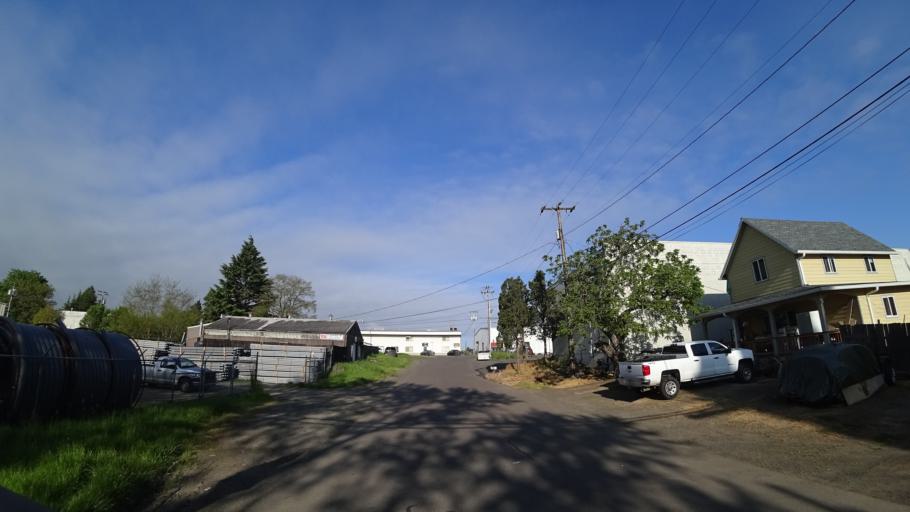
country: US
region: Oregon
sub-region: Washington County
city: Hillsboro
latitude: 45.5143
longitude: -122.9901
